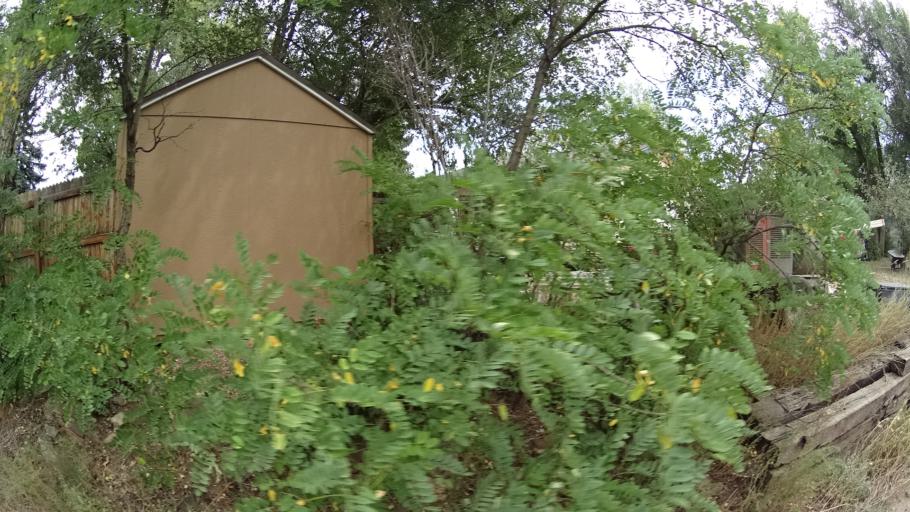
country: US
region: Colorado
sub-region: El Paso County
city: Colorado Springs
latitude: 38.8695
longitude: -104.7915
